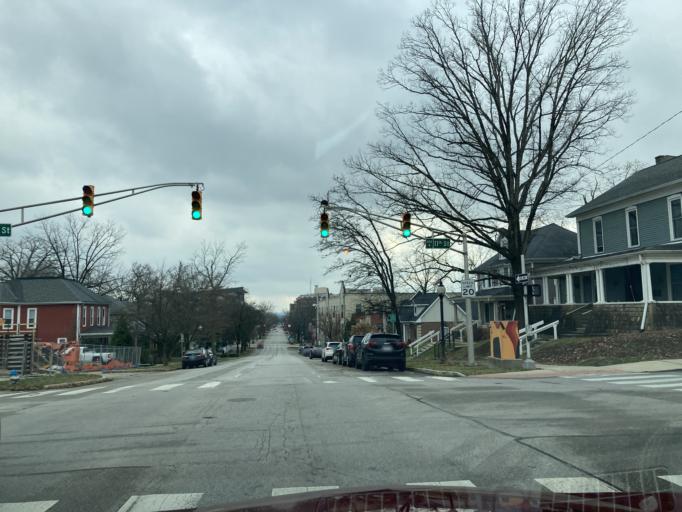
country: US
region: Indiana
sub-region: Monroe County
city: Bloomington
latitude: 39.1734
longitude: -86.5348
